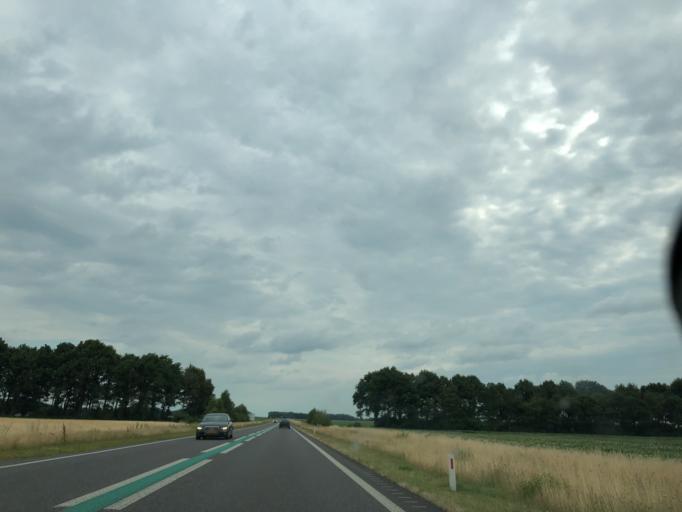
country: NL
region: Drenthe
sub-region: Gemeente Borger-Odoorn
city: Borger
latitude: 52.9412
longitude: 6.7842
